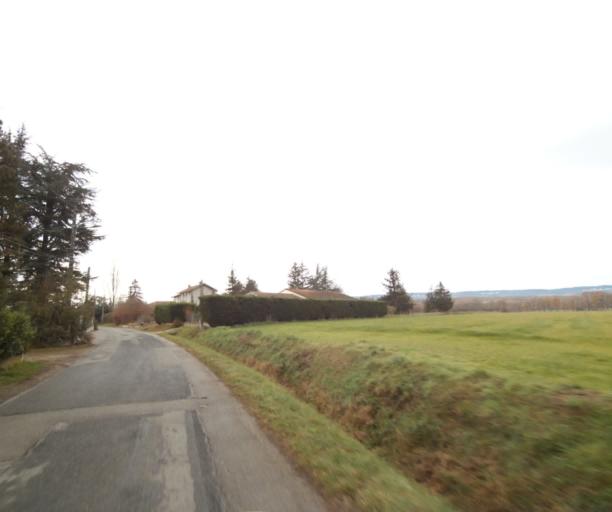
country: FR
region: Rhone-Alpes
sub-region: Departement de la Loire
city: Sury-le-Comtal
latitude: 45.5391
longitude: 4.1684
